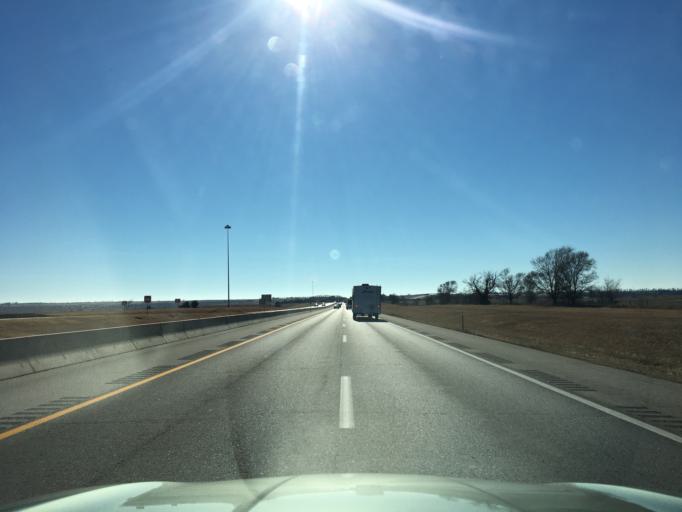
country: US
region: Oklahoma
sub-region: Kay County
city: Blackwell
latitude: 37.0231
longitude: -97.3383
